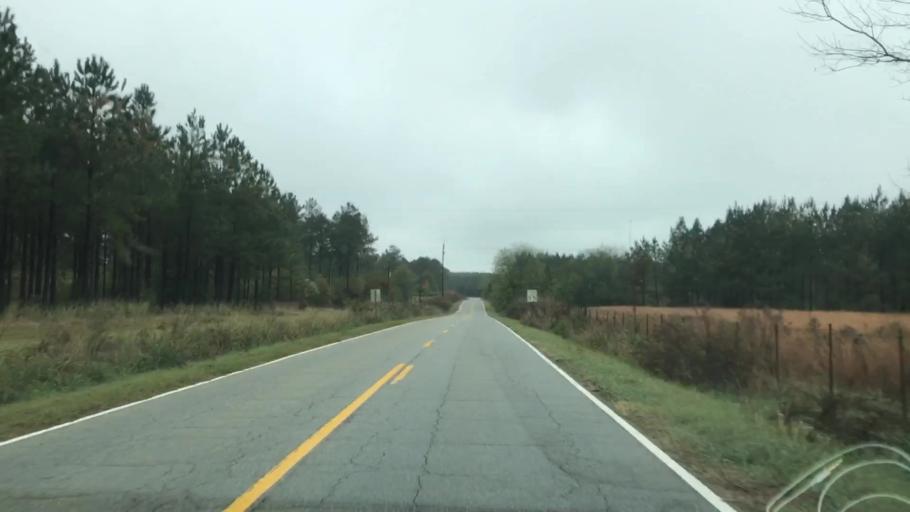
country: US
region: South Carolina
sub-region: Laurens County
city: Joanna
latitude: 34.3779
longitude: -81.7789
